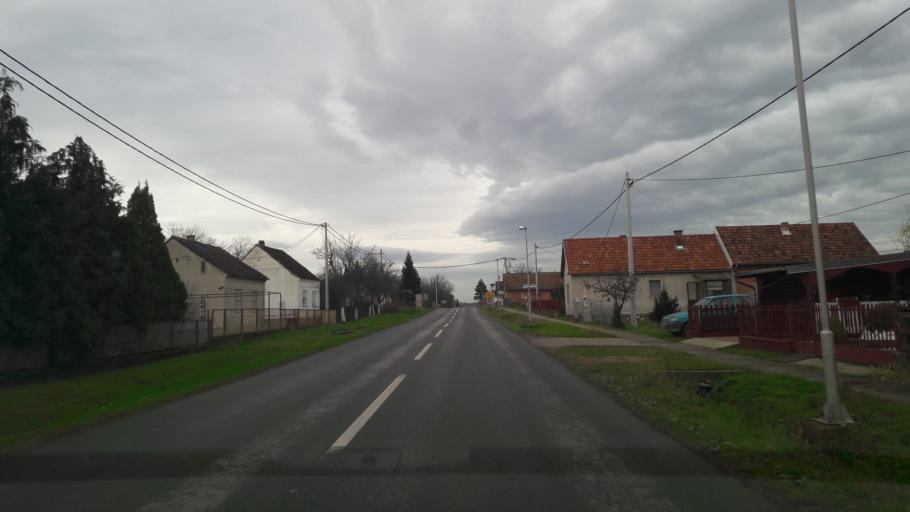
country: HR
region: Osjecko-Baranjska
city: Velimirovac
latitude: 45.5371
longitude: 18.0698
